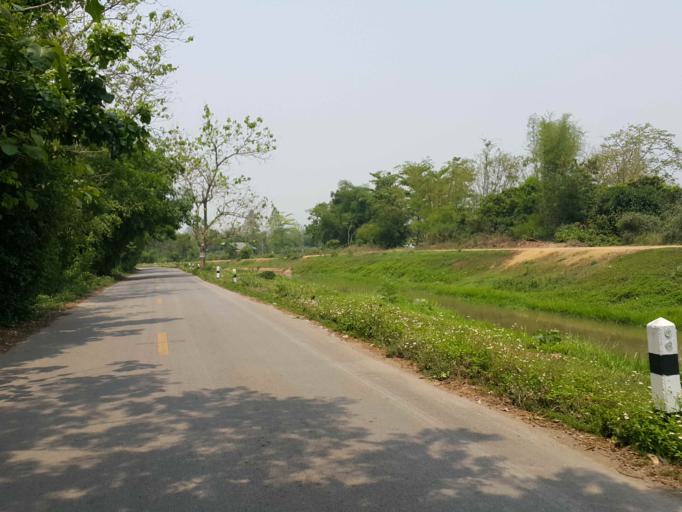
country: TH
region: Chiang Mai
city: San Sai
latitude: 18.8974
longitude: 99.0533
